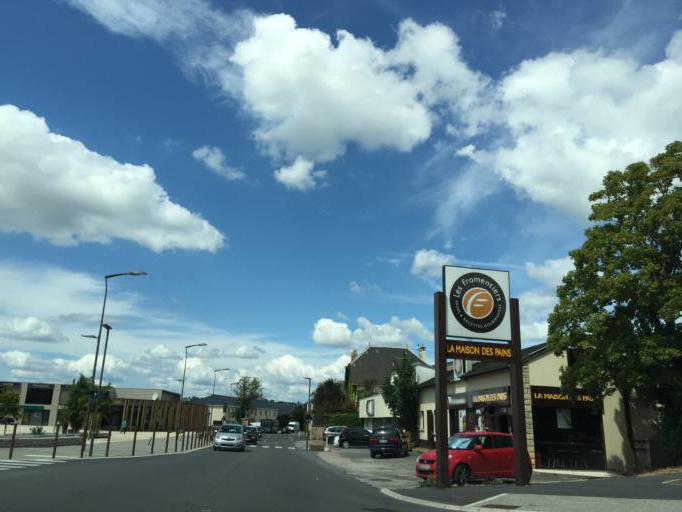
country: FR
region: Midi-Pyrenees
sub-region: Departement de l'Aveyron
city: Rodez
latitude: 44.3641
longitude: 2.5866
